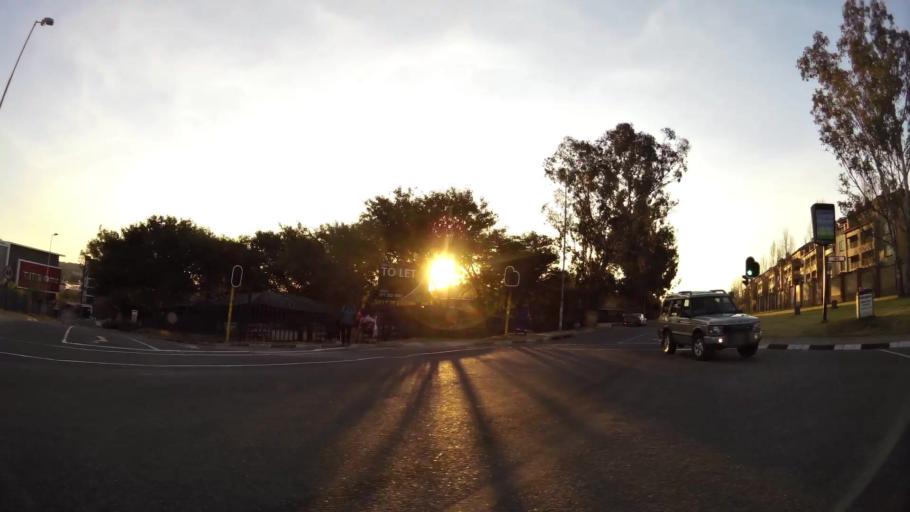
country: ZA
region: Gauteng
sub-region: City of Johannesburg Metropolitan Municipality
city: Midrand
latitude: -26.0351
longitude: 28.0652
